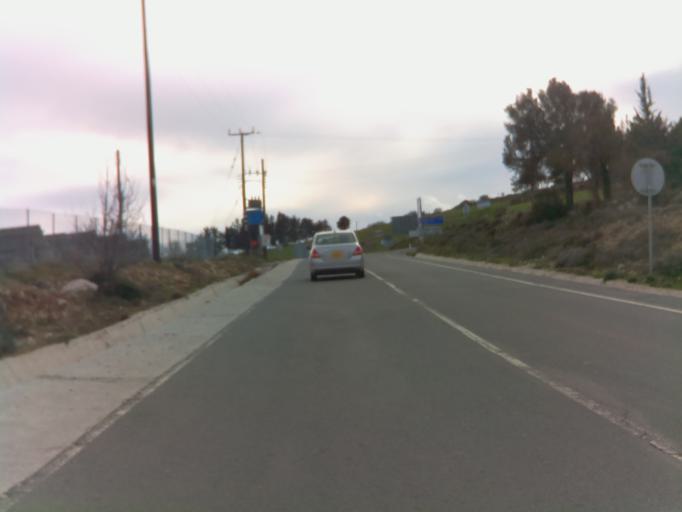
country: CY
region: Pafos
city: Polis
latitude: 34.9597
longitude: 32.4134
